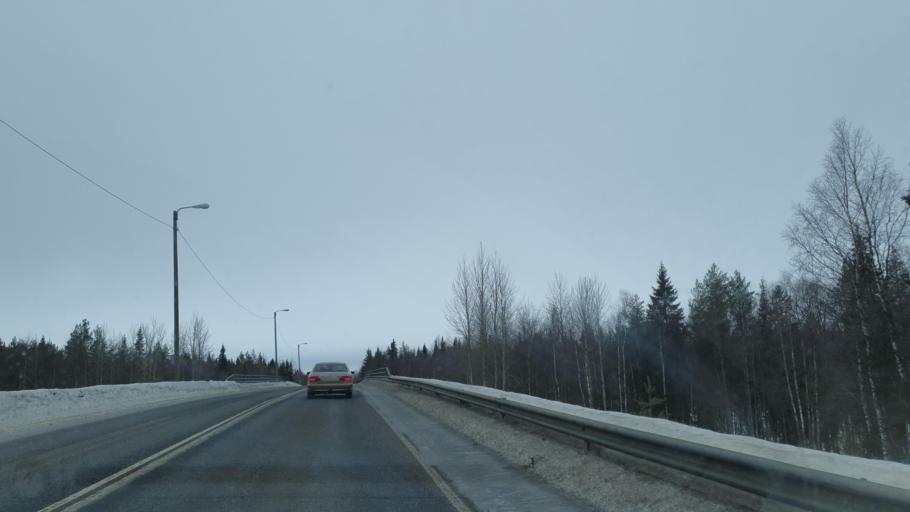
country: SE
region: Norrbotten
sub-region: Overtornea Kommun
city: OEvertornea
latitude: 66.4416
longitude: 23.6844
